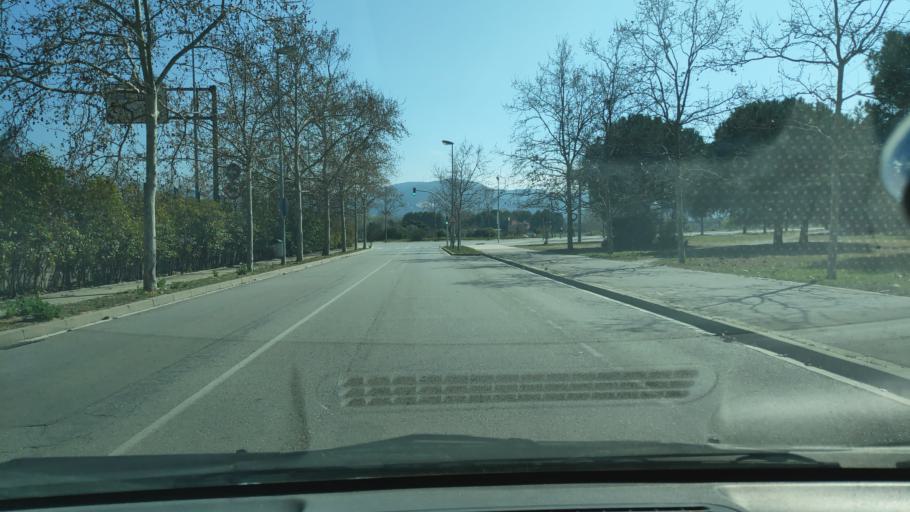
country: ES
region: Catalonia
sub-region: Provincia de Barcelona
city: Santa Perpetua de Mogoda
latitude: 41.5317
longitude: 2.1914
